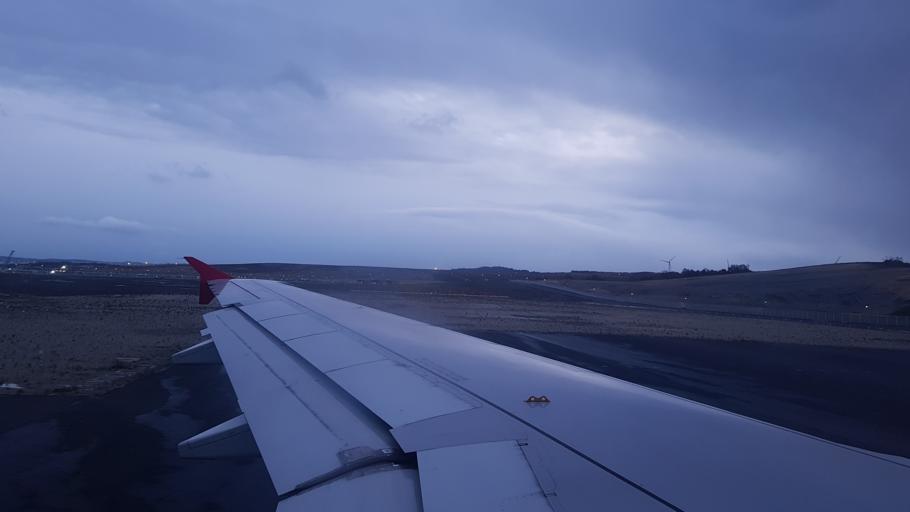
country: TR
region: Istanbul
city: Durusu
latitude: 41.2649
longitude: 28.7077
